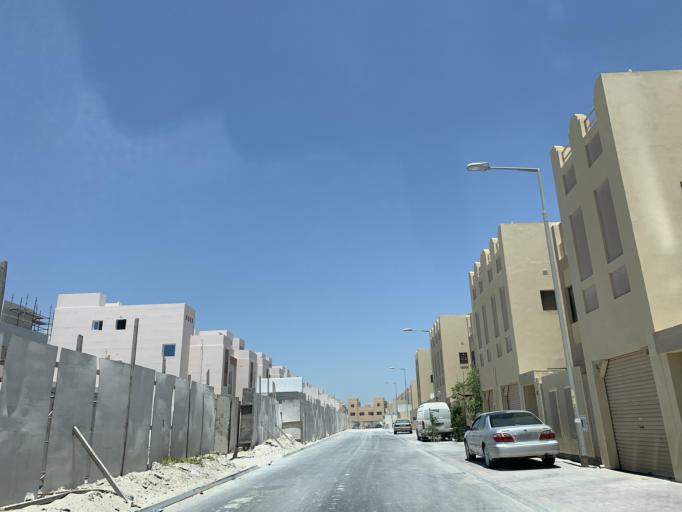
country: BH
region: Manama
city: Jidd Hafs
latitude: 26.2337
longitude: 50.4918
